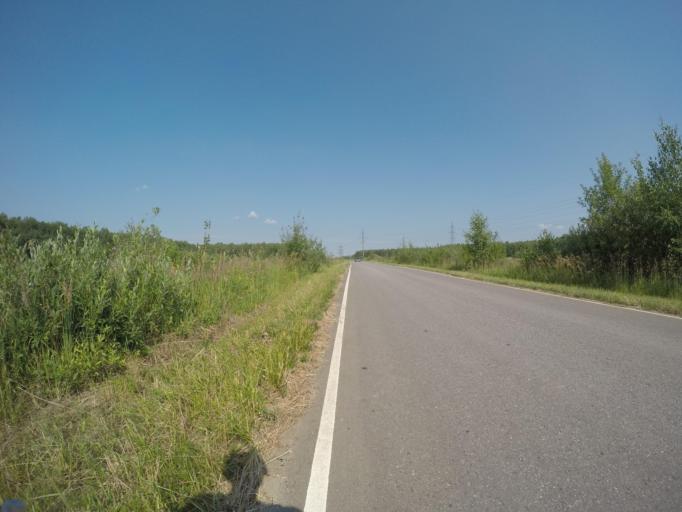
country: RU
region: Moskovskaya
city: Rechitsy
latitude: 55.6236
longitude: 38.5234
